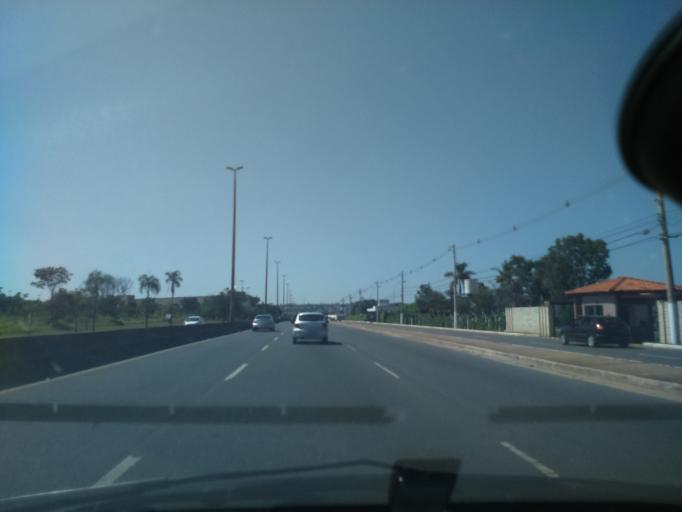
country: BR
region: Federal District
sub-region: Brasilia
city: Brasilia
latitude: -15.8138
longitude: -47.8423
